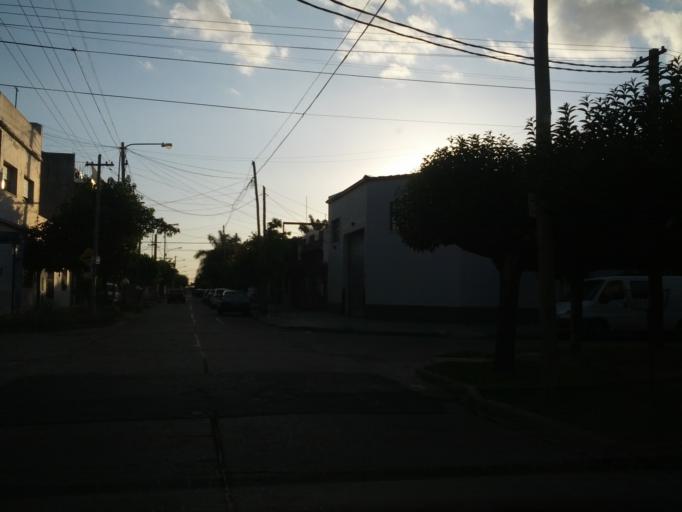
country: AR
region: Buenos Aires
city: San Justo
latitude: -34.6536
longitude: -58.5397
